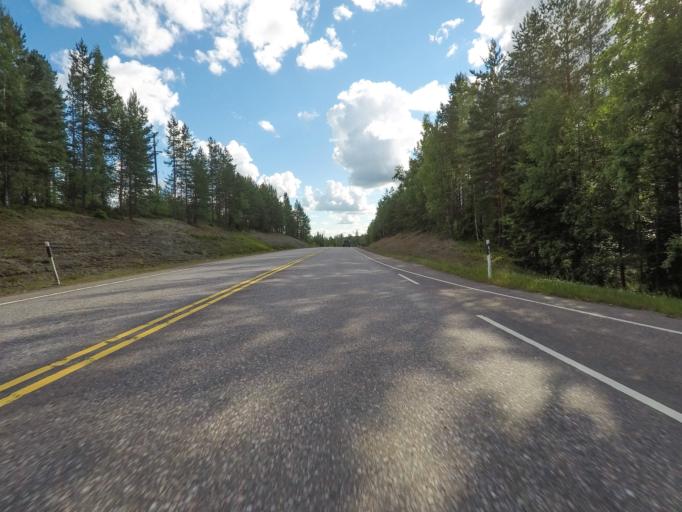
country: FI
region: Uusimaa
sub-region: Helsinki
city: Nurmijaervi
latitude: 60.5161
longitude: 24.6475
